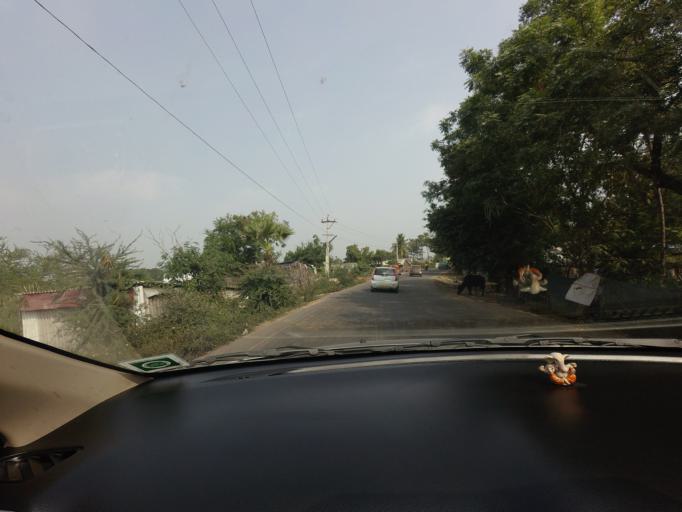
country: IN
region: Andhra Pradesh
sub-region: Krishna
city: Kankipadu
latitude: 16.4563
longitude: 80.7960
